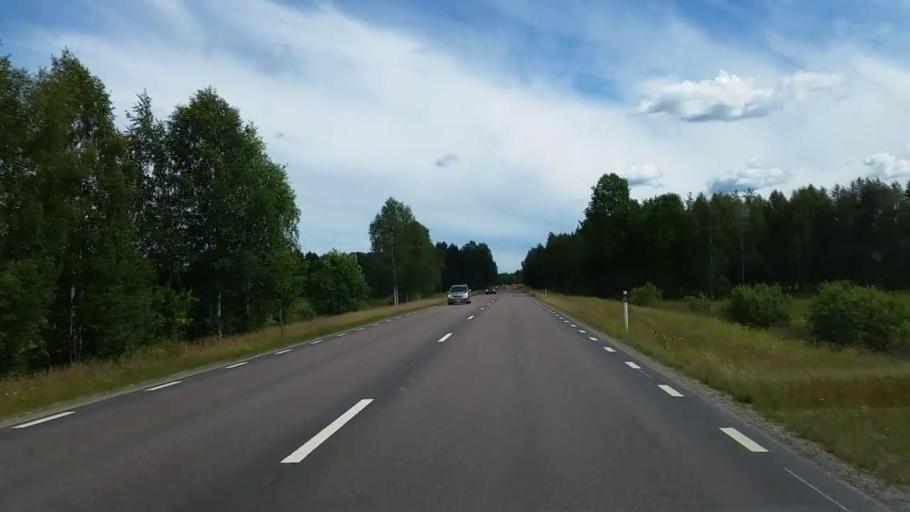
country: SE
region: Gaevleborg
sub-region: Ovanakers Kommun
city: Edsbyn
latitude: 61.3693
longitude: 15.8605
